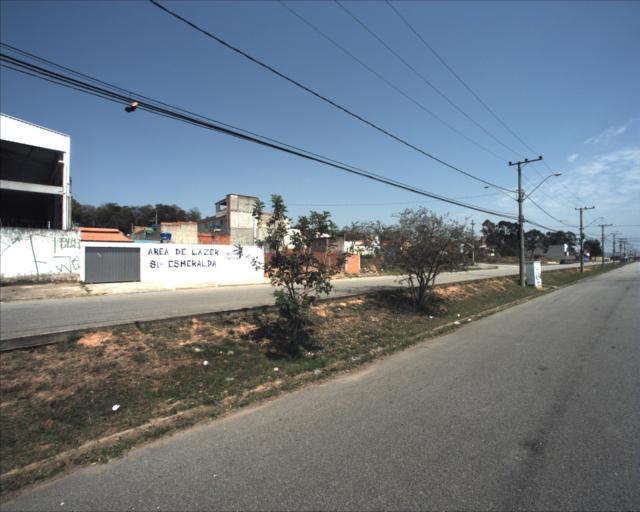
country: BR
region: Sao Paulo
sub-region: Sorocaba
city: Sorocaba
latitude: -23.4363
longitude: -47.4797
